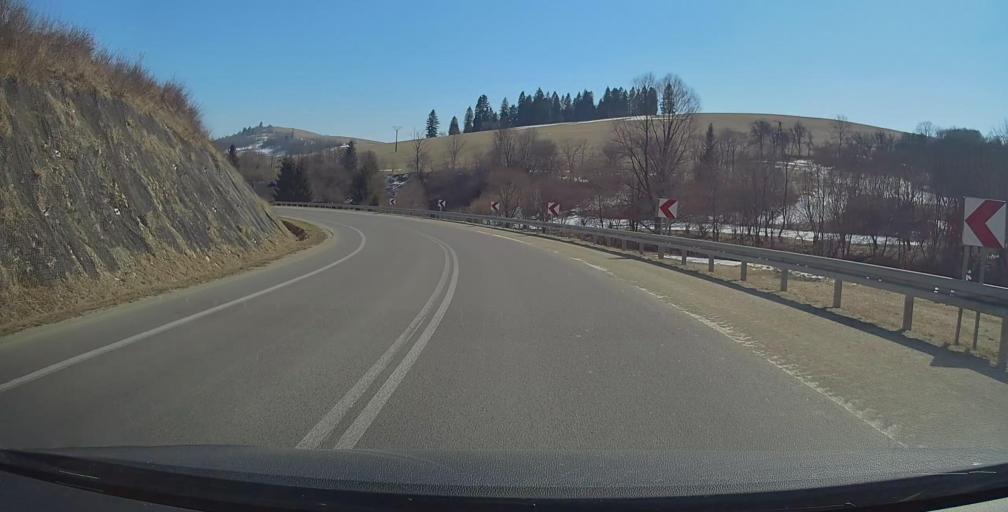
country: PL
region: Subcarpathian Voivodeship
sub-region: Powiat bieszczadzki
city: Ustrzyki Dolne
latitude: 49.4958
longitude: 22.6345
